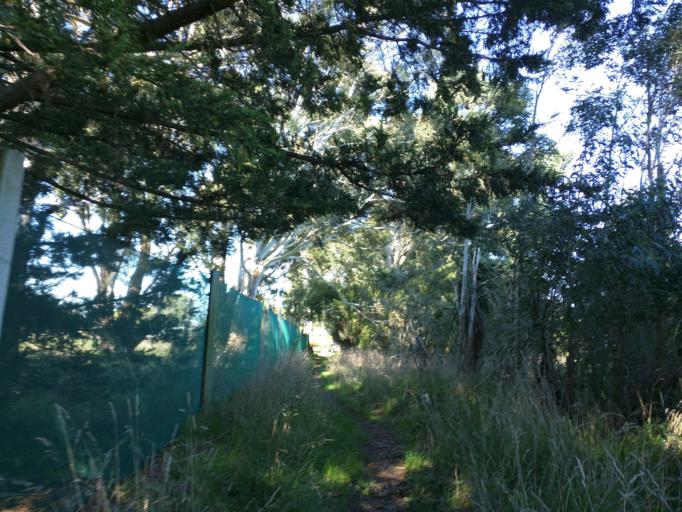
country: NZ
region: Canterbury
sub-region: Selwyn District
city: Lincoln
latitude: -43.6452
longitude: 172.4594
